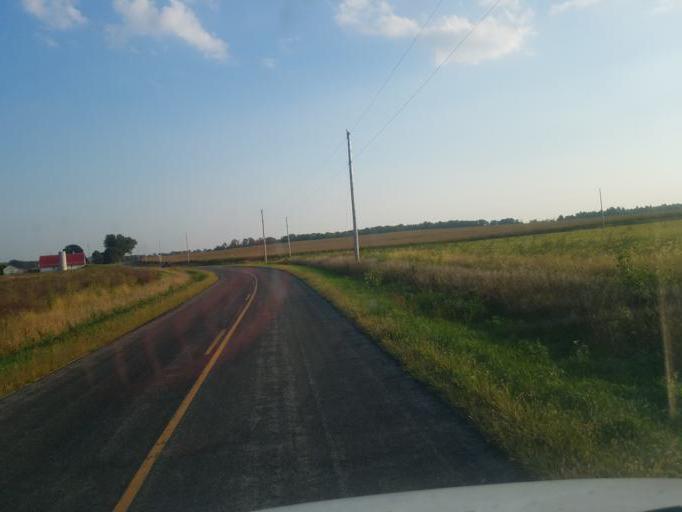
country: US
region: Ohio
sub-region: Crawford County
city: Bucyrus
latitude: 40.8865
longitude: -82.8778
